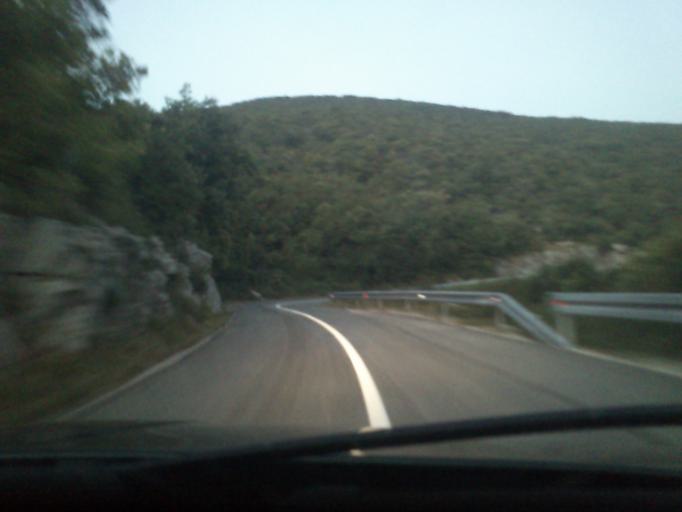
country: HR
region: Licko-Senjska
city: Senj
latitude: 44.8995
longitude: 14.9574
